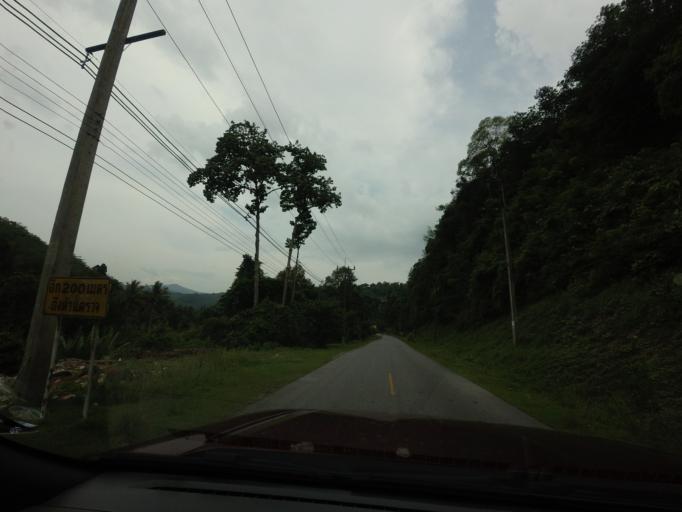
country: TH
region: Yala
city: Than To
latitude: 6.1646
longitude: 101.2685
